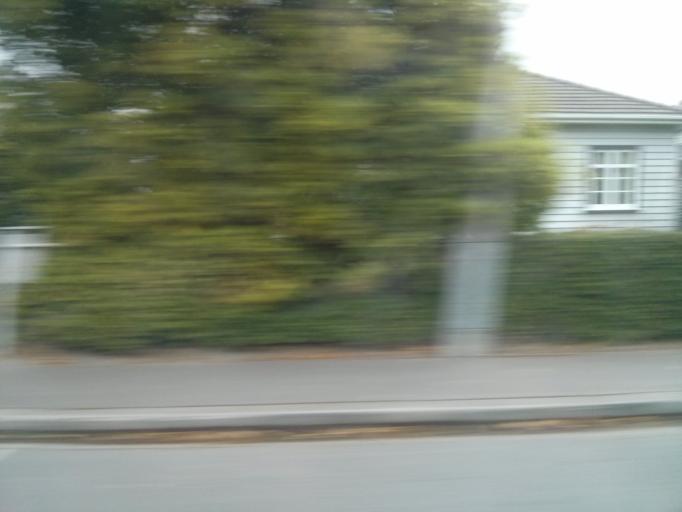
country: NZ
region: Canterbury
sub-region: Christchurch City
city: Christchurch
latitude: -43.5249
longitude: 172.6024
